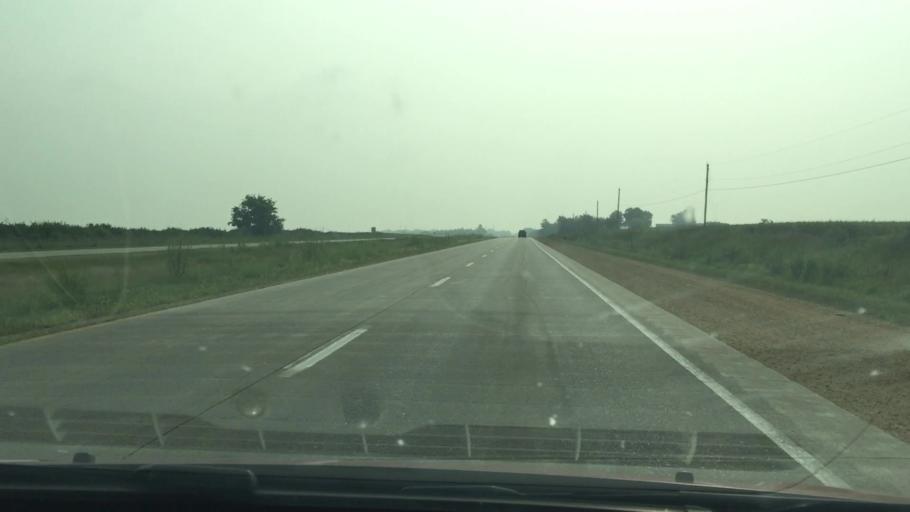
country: US
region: Iowa
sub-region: Scott County
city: Blue Grass
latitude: 41.5089
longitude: -90.7252
